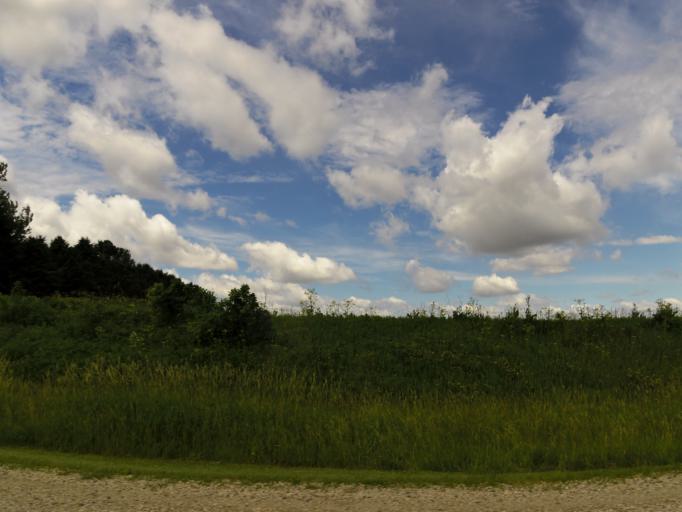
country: US
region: Iowa
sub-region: Chickasaw County
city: New Hampton
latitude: 43.1868
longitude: -92.2983
